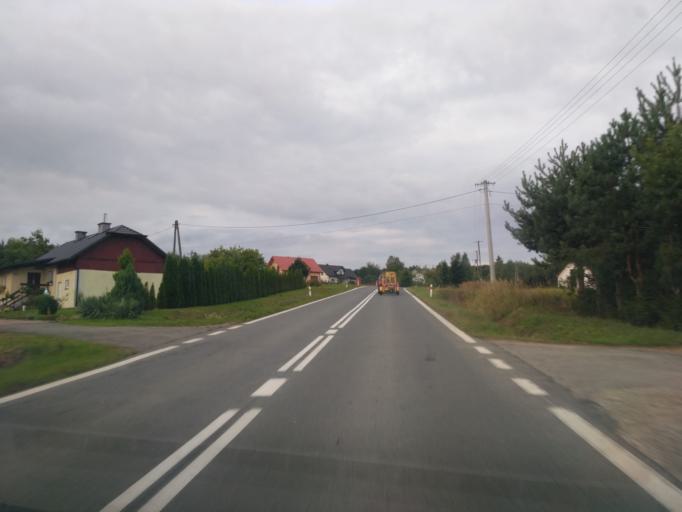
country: PL
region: Subcarpathian Voivodeship
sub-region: Powiat jasielski
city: Tarnowiec
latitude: 49.7889
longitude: 21.5701
